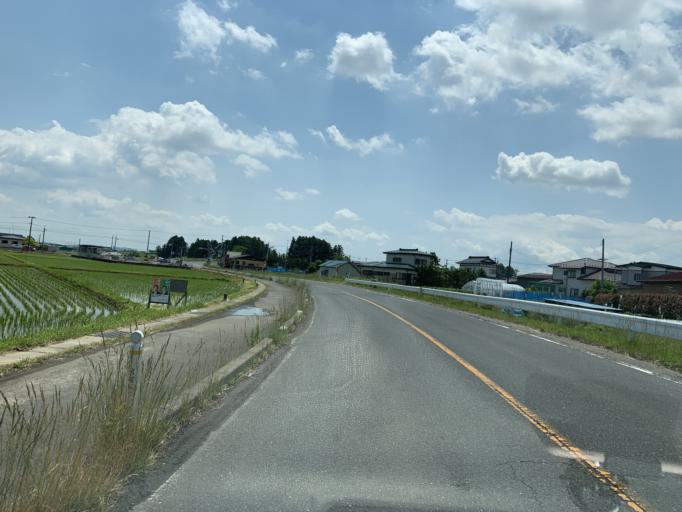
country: JP
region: Miyagi
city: Kogota
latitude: 38.5323
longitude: 141.0550
